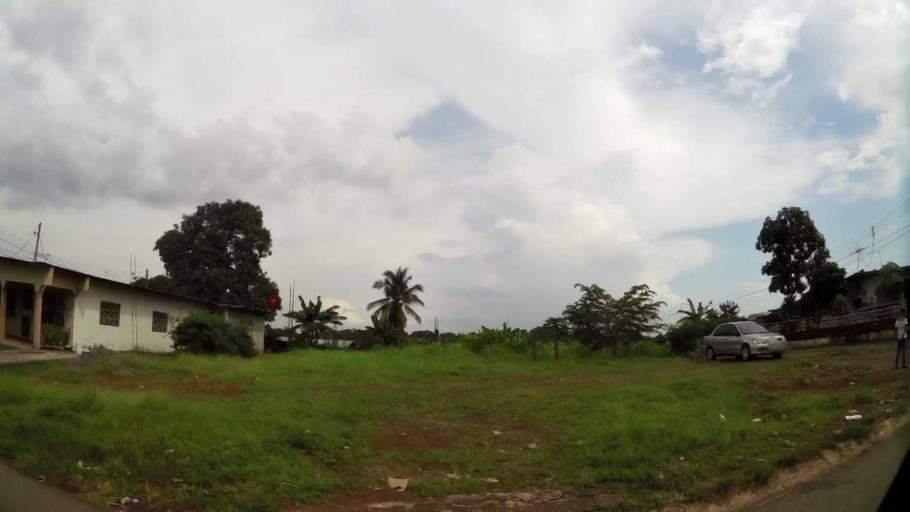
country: PA
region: Panama
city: Tocumen
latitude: 9.1007
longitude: -79.3669
